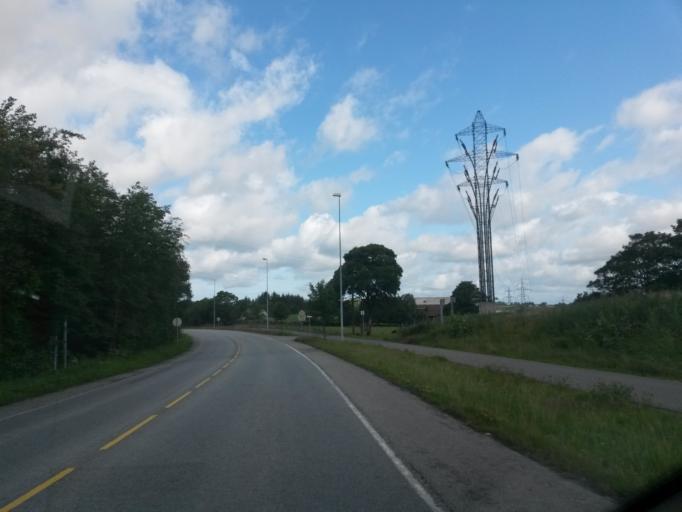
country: NO
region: Rogaland
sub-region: Sandnes
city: Sandnes
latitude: 58.8606
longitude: 5.7053
